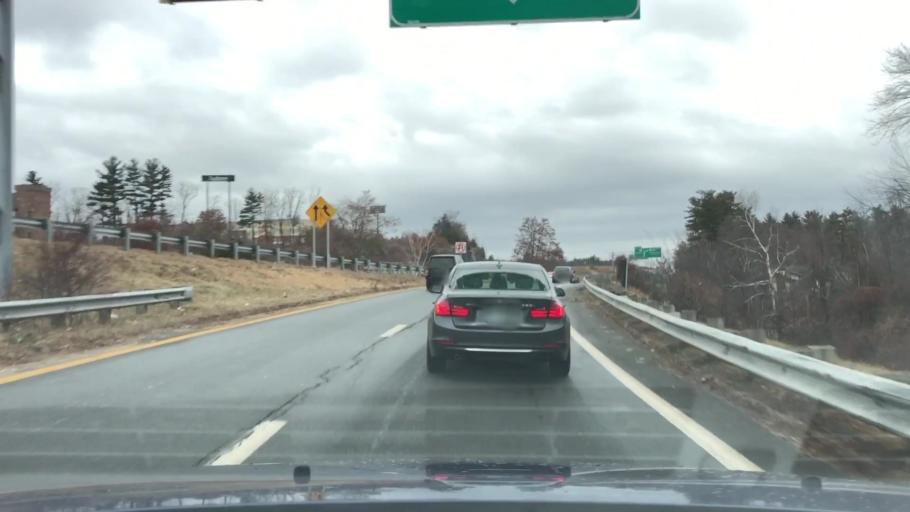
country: US
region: Massachusetts
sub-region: Middlesex County
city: Tyngsboro
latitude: 42.7090
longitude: -71.4497
